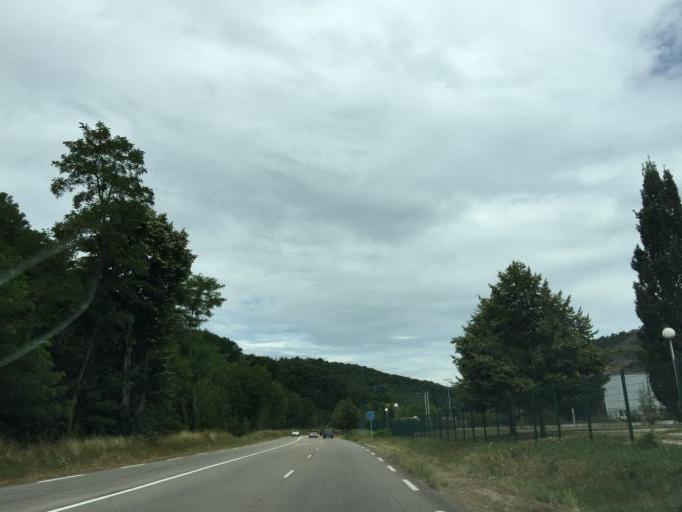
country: FR
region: Rhone-Alpes
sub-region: Departement de la Loire
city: Fraisses
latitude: 45.3998
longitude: 4.2568
